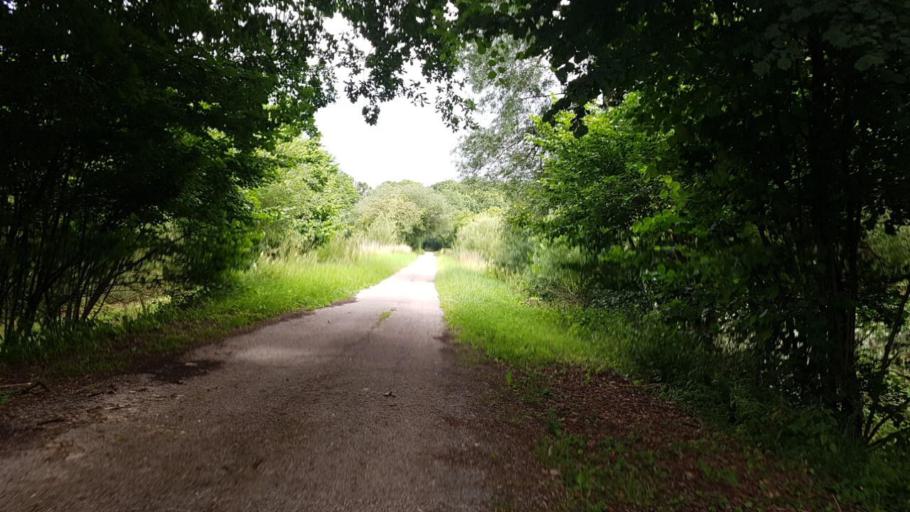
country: FR
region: Picardie
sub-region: Departement de l'Aisne
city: Esqueheries
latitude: 49.9024
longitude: 3.7569
